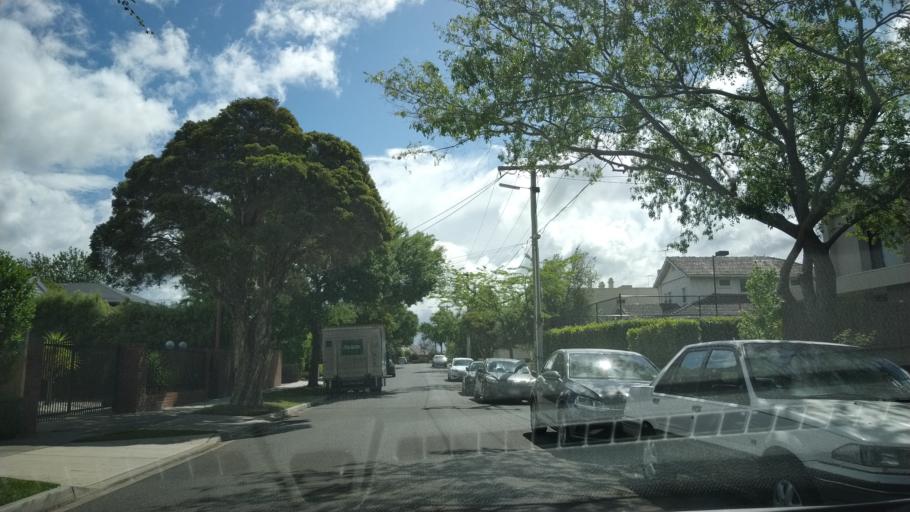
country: AU
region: Victoria
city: Caulfield North
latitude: -37.8796
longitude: 145.0322
